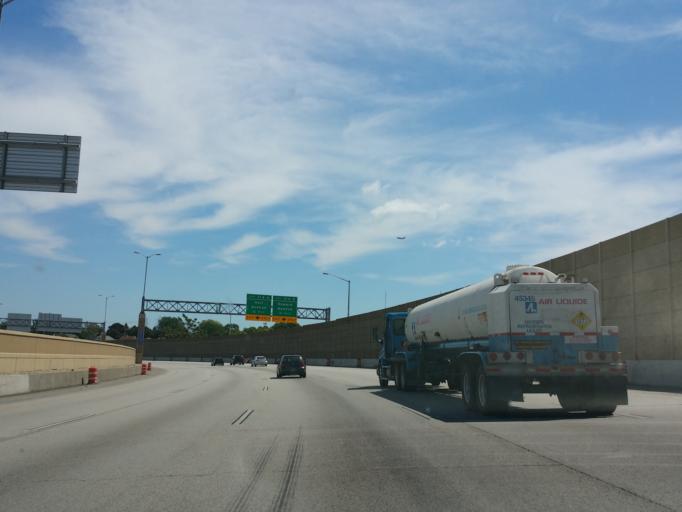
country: US
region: Wisconsin
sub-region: Milwaukee County
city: Saint Francis
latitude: 42.9668
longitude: -87.9182
